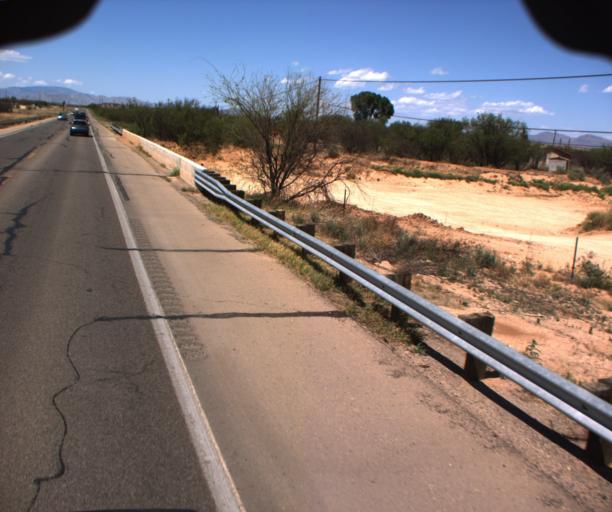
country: US
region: Arizona
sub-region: Cochise County
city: Saint David
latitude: 31.9132
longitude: -110.2605
